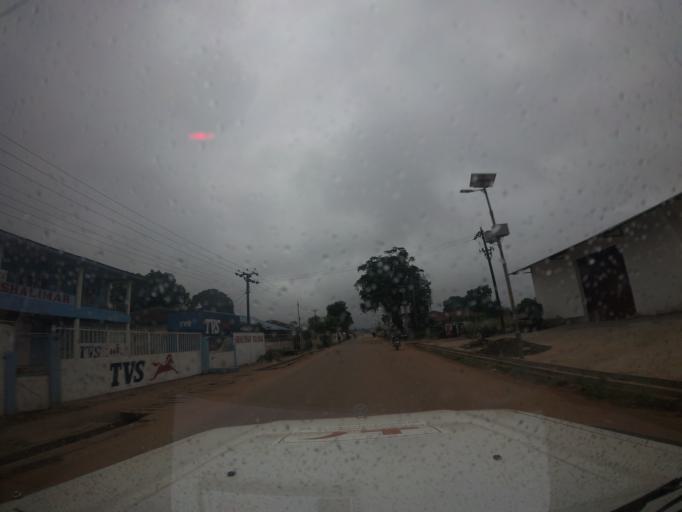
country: SL
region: Eastern Province
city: Kenema
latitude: 7.8867
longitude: -11.1883
